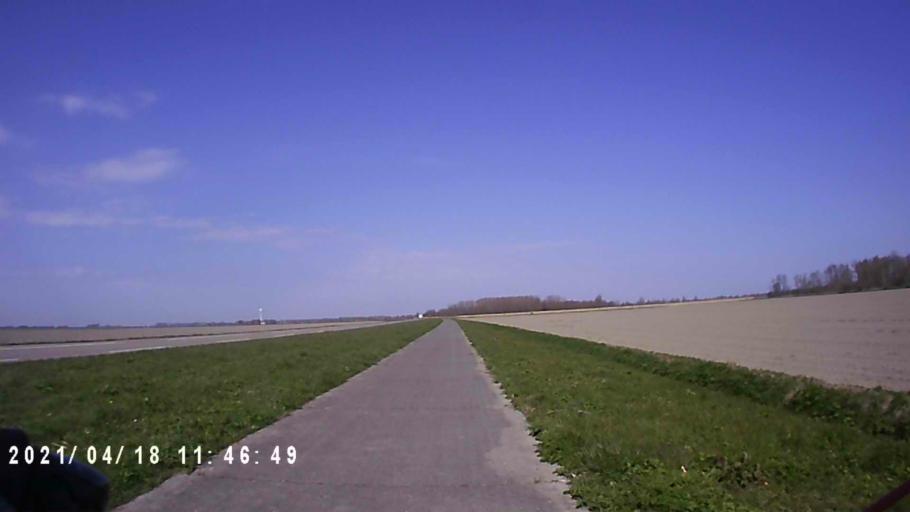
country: NL
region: Groningen
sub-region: Gemeente Zuidhorn
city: Grijpskerk
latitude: 53.3202
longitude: 6.2557
